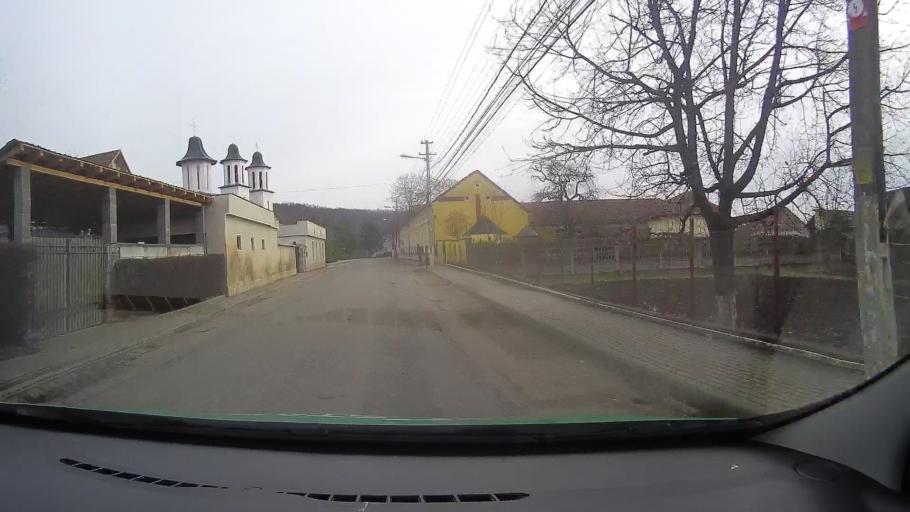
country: RO
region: Hunedoara
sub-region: Comuna Geoagiu
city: Geoagiu
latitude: 45.9252
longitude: 23.1980
